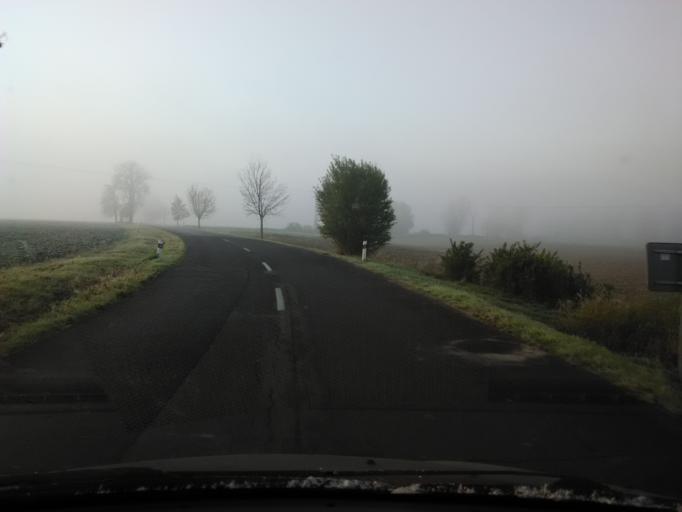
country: SK
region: Nitriansky
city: Tlmace
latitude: 48.2648
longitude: 18.5362
